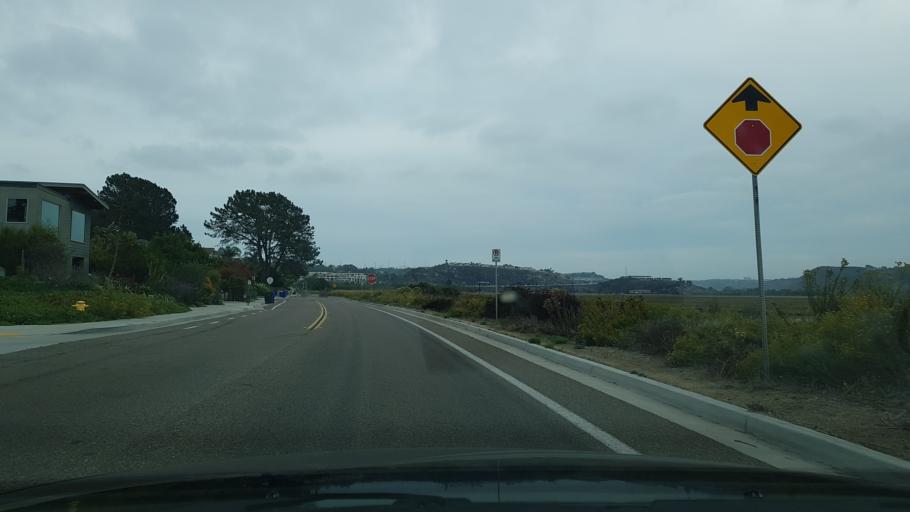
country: US
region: California
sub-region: San Diego County
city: Del Mar
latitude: 32.9321
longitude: -117.2511
